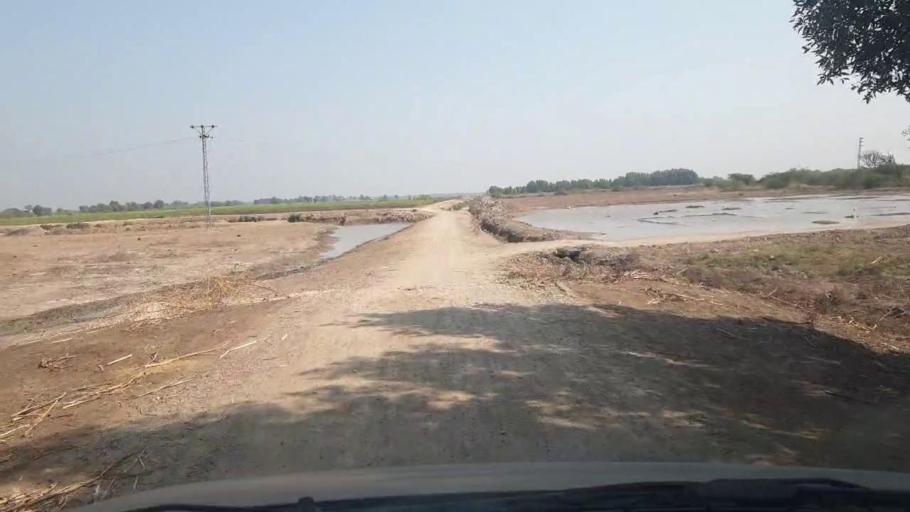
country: PK
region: Sindh
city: Digri
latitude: 25.2319
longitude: 69.1617
